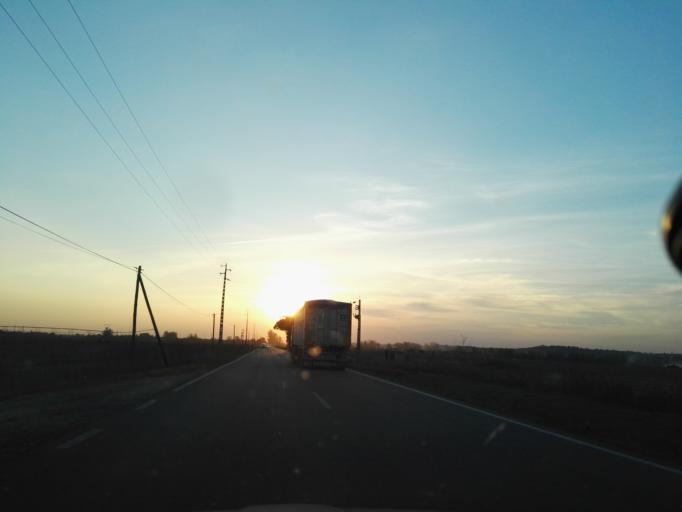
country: PT
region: Santarem
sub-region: Coruche
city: Coruche
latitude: 38.9738
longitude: -8.4587
